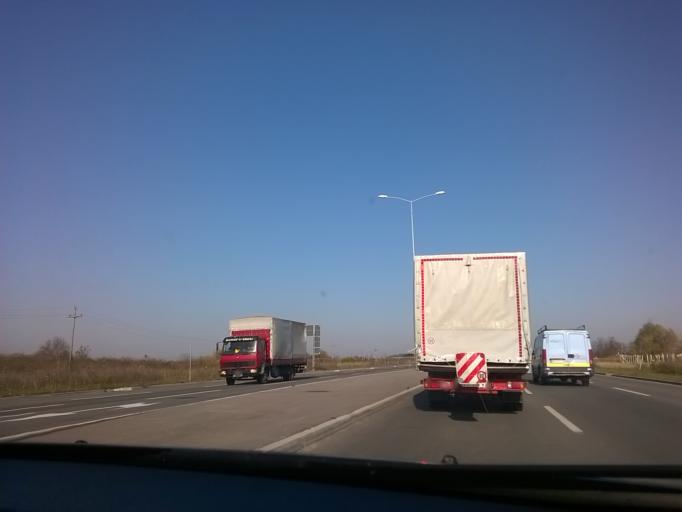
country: RS
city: Ovca
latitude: 44.8512
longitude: 20.5170
